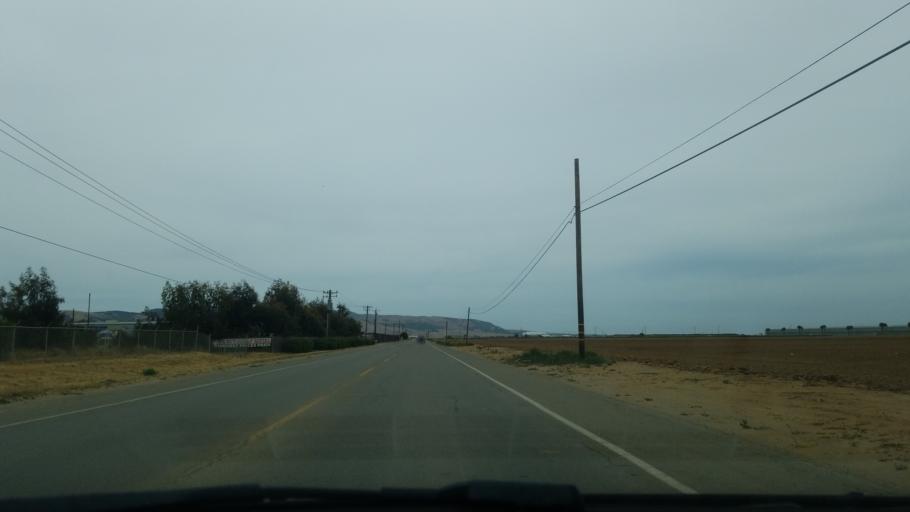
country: US
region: California
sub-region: Santa Barbara County
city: Santa Maria
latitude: 34.9213
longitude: -120.4797
